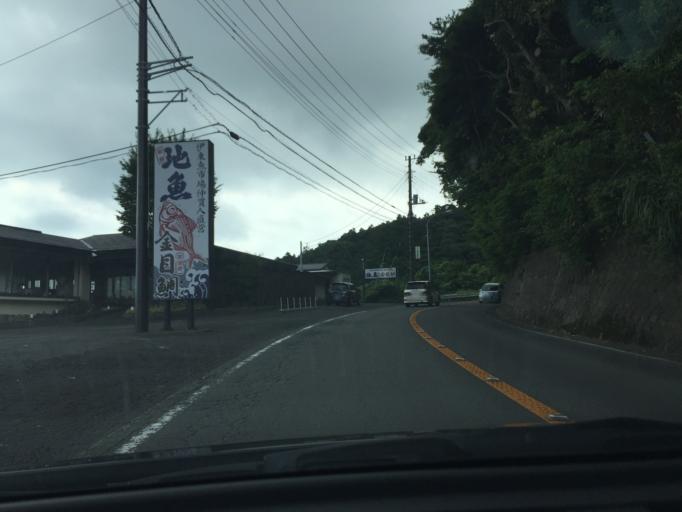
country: JP
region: Shizuoka
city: Ito
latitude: 34.9290
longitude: 139.1282
